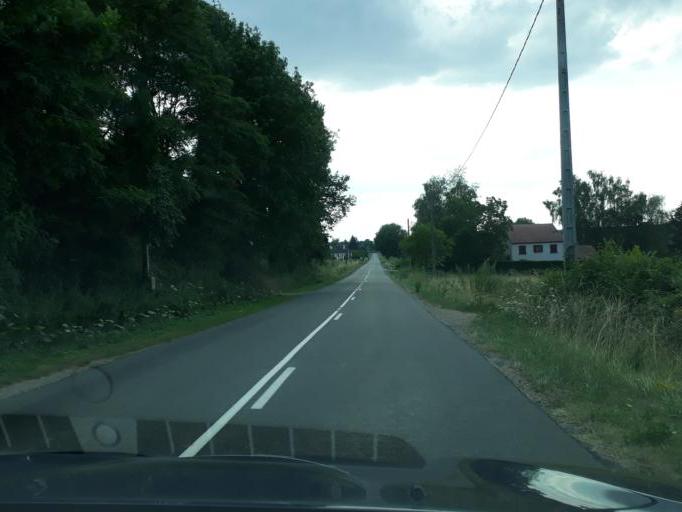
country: FR
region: Centre
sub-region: Departement du Cher
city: Cours-les-Barres
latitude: 46.9826
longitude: 2.9900
